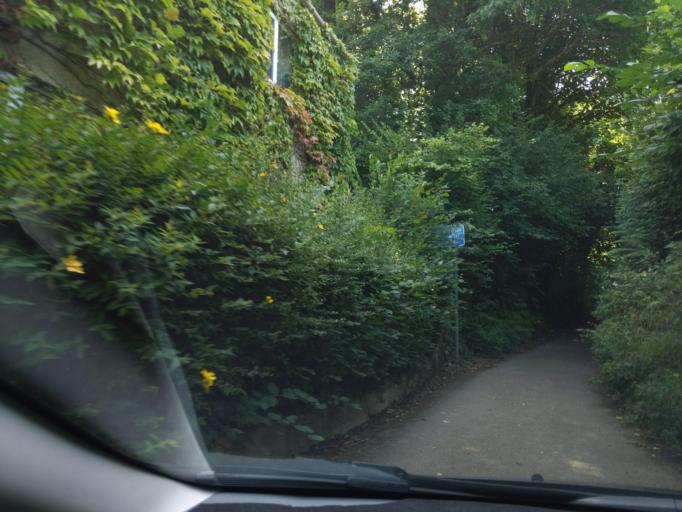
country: GB
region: England
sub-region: Devon
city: Plympton
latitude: 50.3820
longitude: -4.0511
